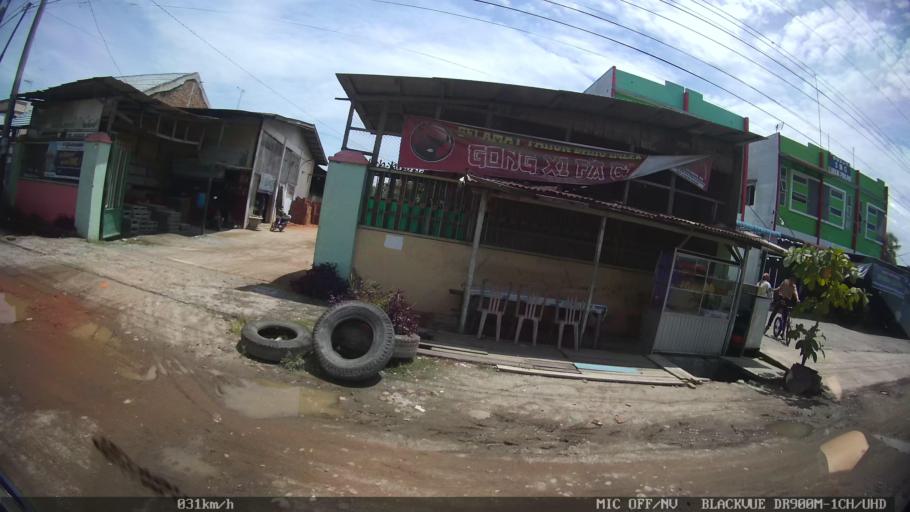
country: ID
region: North Sumatra
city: Perbaungan
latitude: 3.5455
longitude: 98.8803
